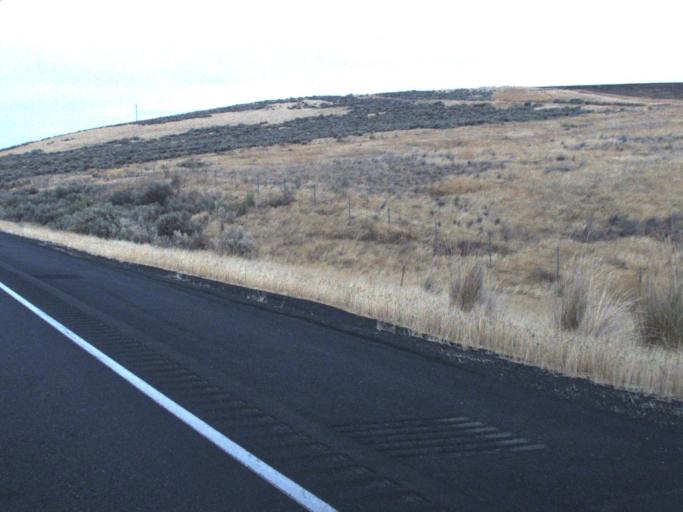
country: US
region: Washington
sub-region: Grant County
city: Warden
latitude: 47.0846
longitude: -118.9738
